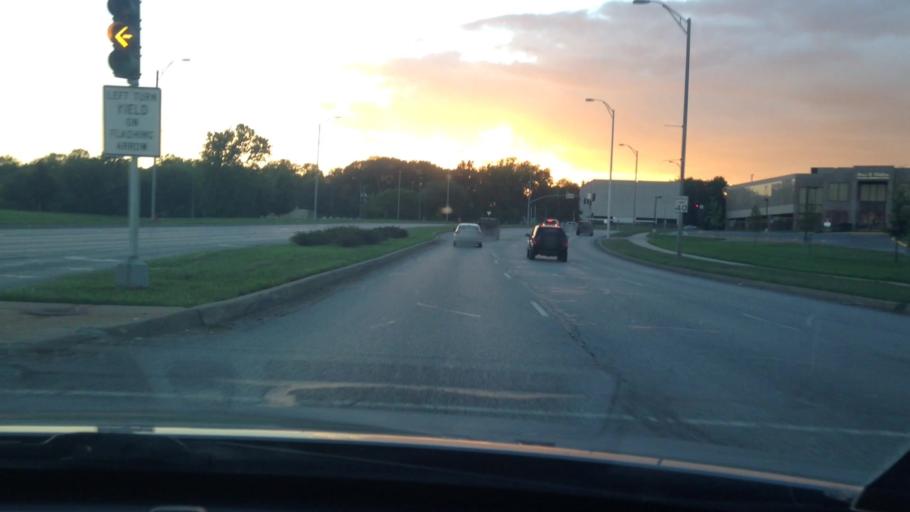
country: US
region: Missouri
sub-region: Jackson County
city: Kansas City
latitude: 39.0362
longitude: -94.5409
